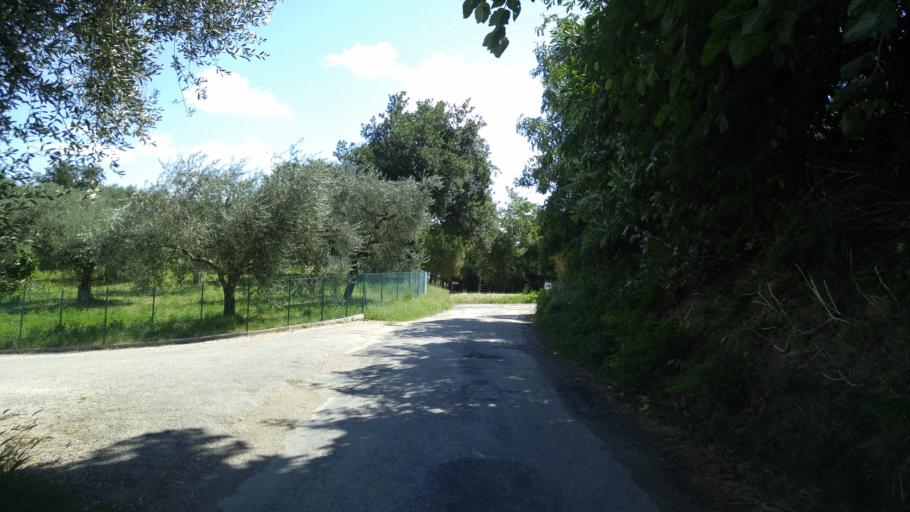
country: IT
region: The Marches
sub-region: Provincia di Pesaro e Urbino
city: Centinarola
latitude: 43.8214
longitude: 12.9759
